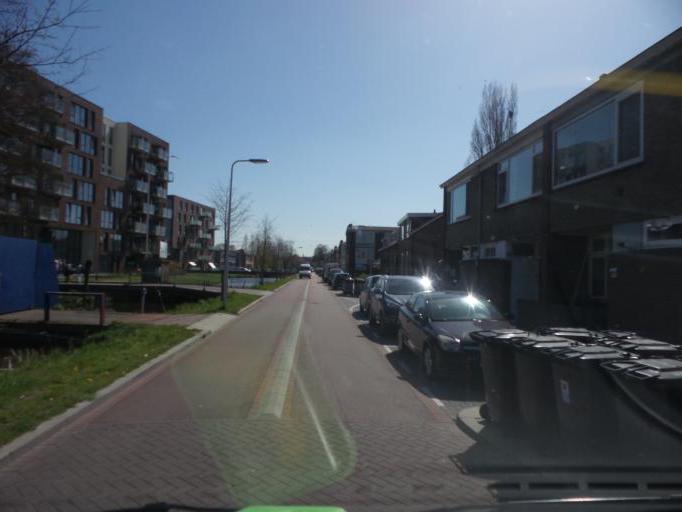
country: NL
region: South Holland
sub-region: Gemeente Gouda
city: Gouda
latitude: 52.0163
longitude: 4.6974
